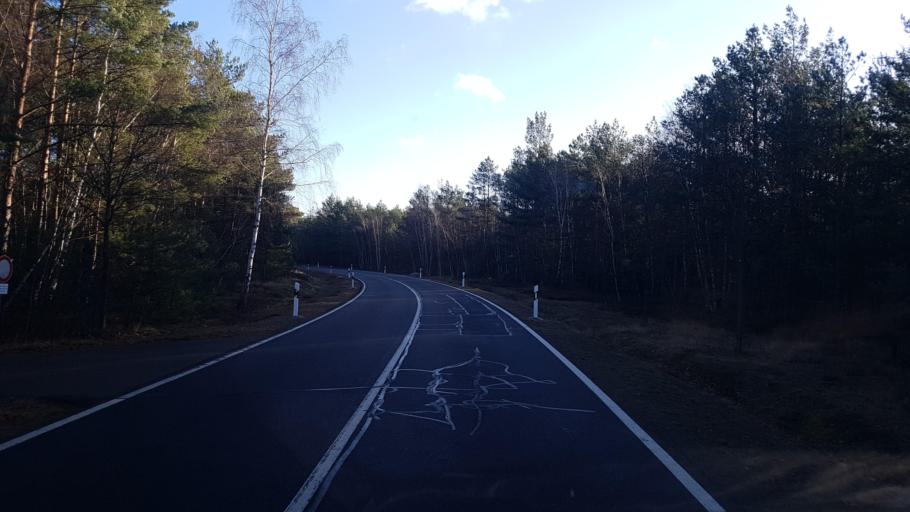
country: DE
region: Brandenburg
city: Heinersbruck
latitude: 51.7487
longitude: 14.5545
